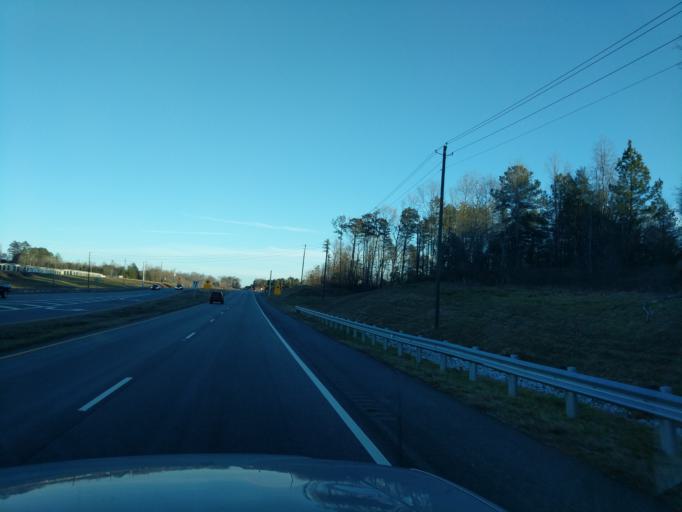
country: US
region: Georgia
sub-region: Stephens County
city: Toccoa
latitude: 34.5236
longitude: -83.2464
